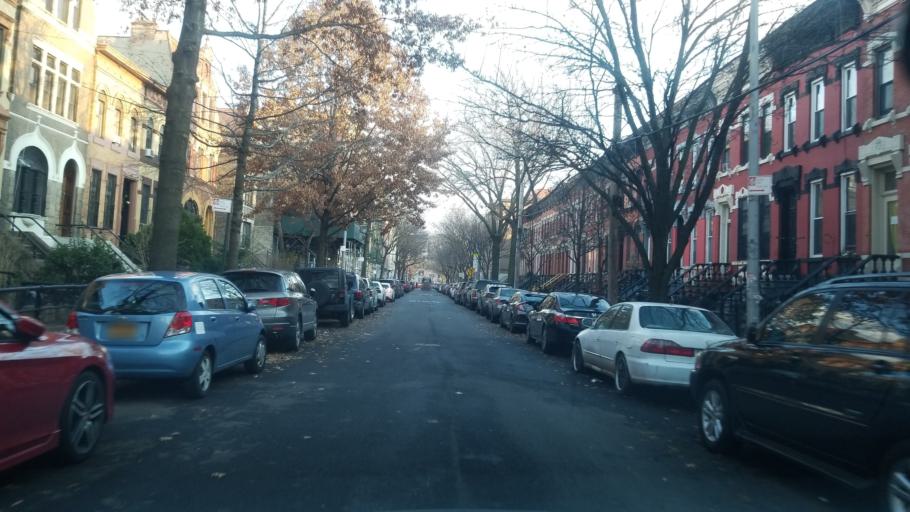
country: US
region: New York
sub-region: New York County
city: Manhattan
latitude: 40.8102
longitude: -73.9214
